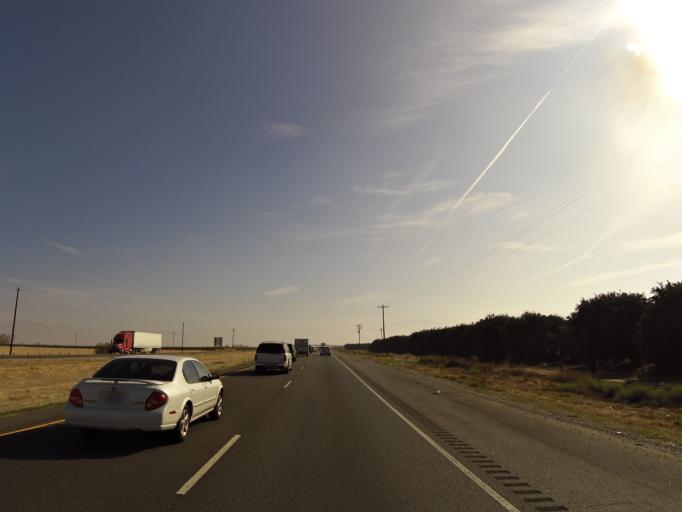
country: US
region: California
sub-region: Kern County
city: Weedpatch
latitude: 35.0468
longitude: -118.9863
